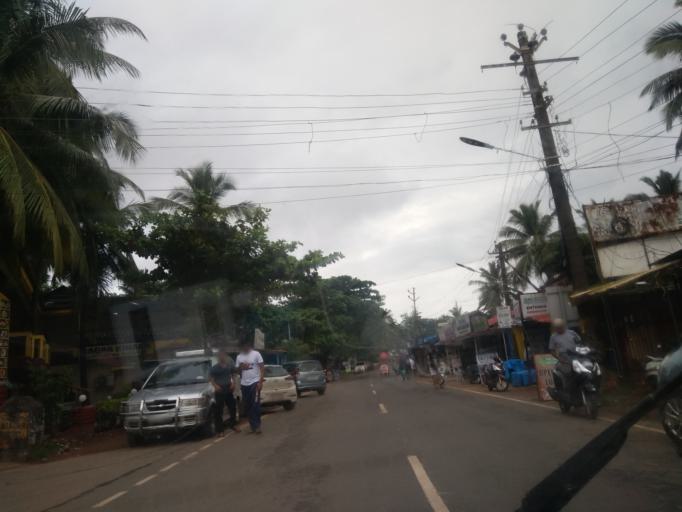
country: IN
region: Goa
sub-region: South Goa
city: Colva
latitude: 15.2765
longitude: 73.9165
